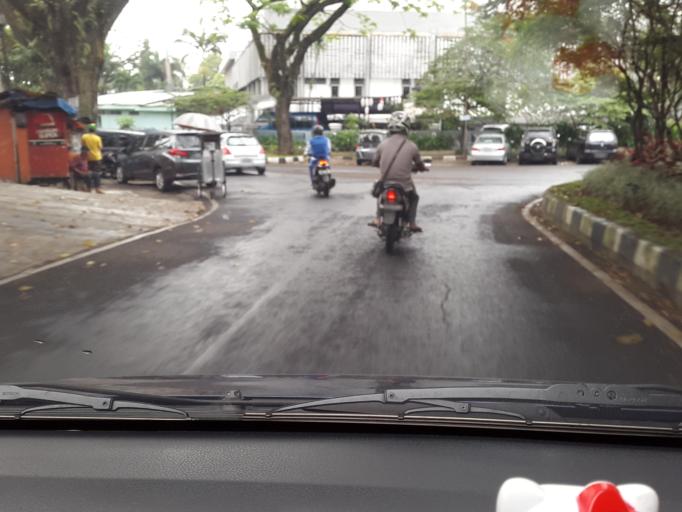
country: ID
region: West Java
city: Bandung
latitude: -6.9041
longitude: 107.6209
